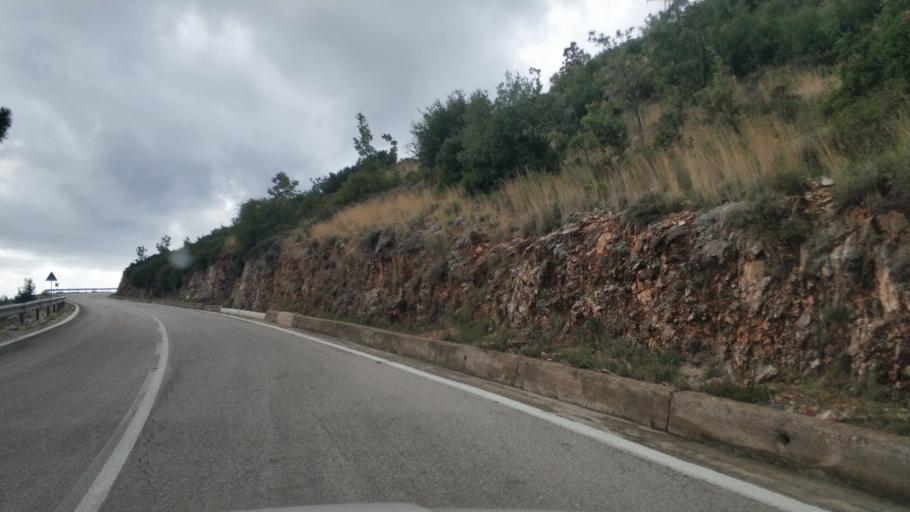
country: AL
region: Vlore
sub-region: Rrethi i Vlores
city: Vranisht
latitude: 40.1457
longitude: 19.6594
